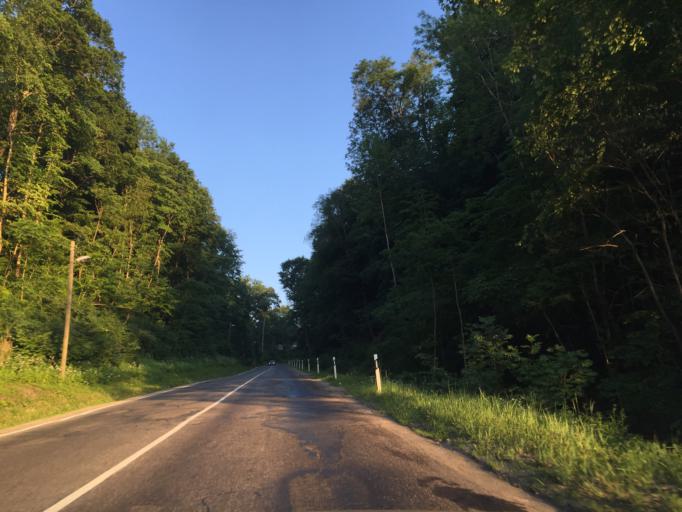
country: LV
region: Sigulda
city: Sigulda
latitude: 57.1653
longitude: 24.8486
